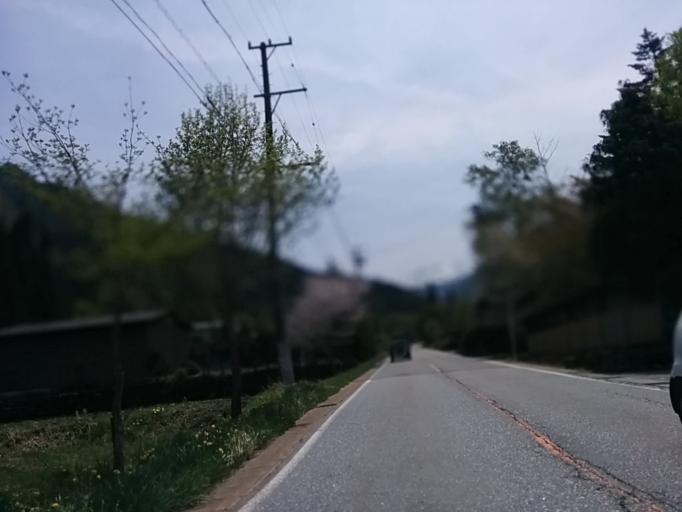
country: JP
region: Gifu
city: Takayama
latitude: 36.2332
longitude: 137.5333
